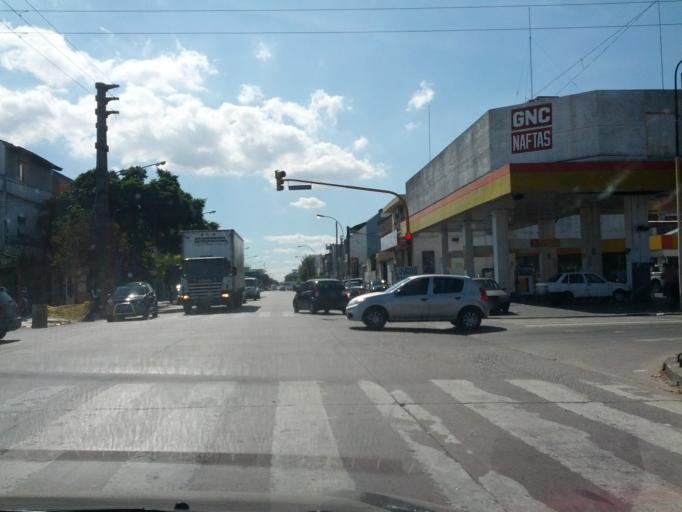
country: AR
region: Buenos Aires
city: San Justo
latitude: -34.6518
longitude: -58.5328
